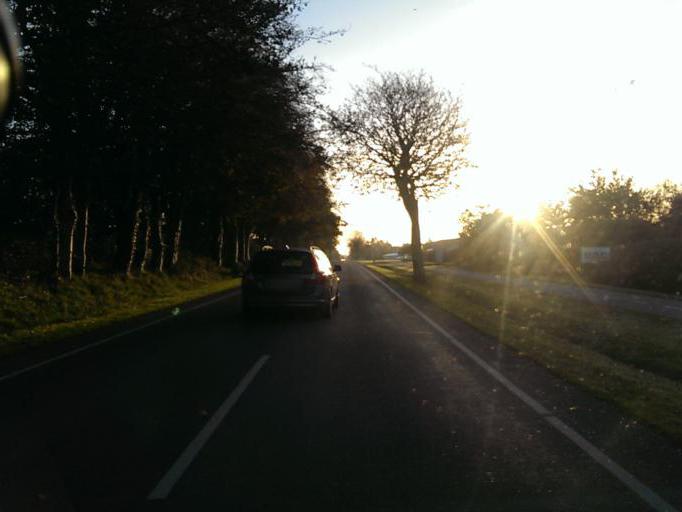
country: DK
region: South Denmark
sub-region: Esbjerg Kommune
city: Bramming
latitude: 55.4688
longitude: 8.6762
